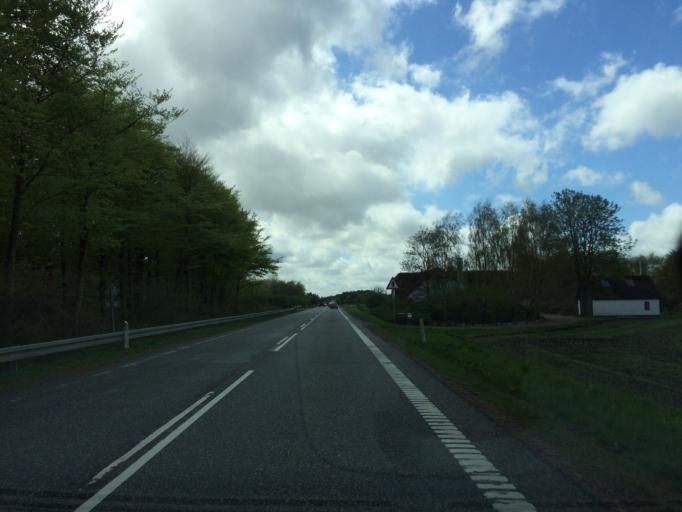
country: DK
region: Central Jutland
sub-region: Viborg Kommune
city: Stoholm
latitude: 56.4227
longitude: 9.0534
